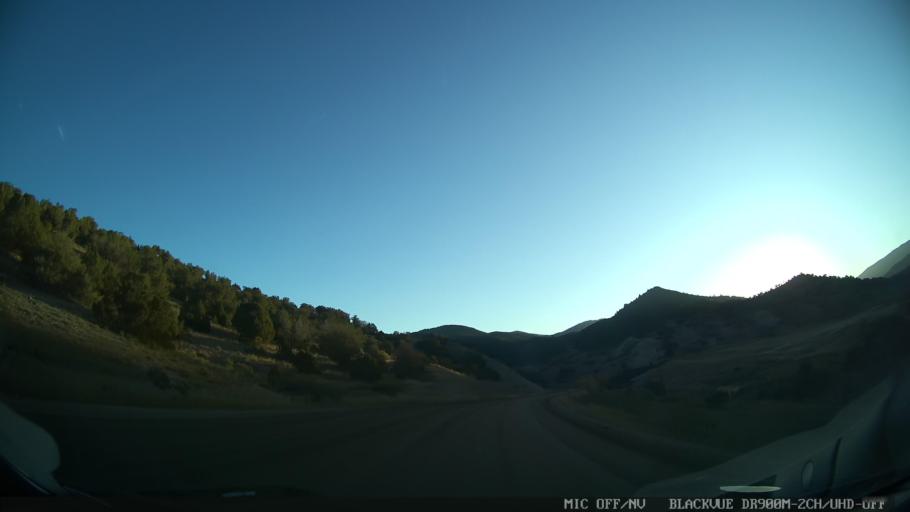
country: US
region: Colorado
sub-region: Grand County
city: Kremmling
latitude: 39.9253
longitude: -106.5336
